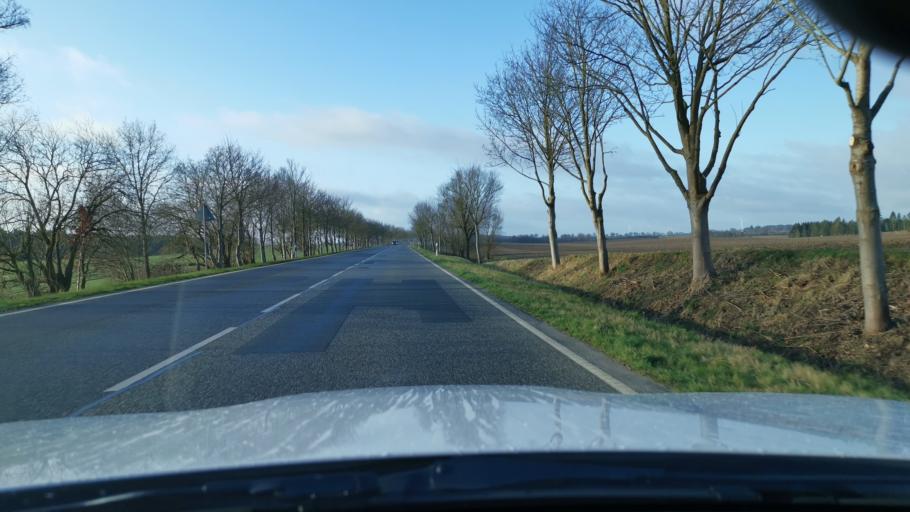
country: DE
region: Mecklenburg-Vorpommern
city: Laage
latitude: 53.9116
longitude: 12.3164
